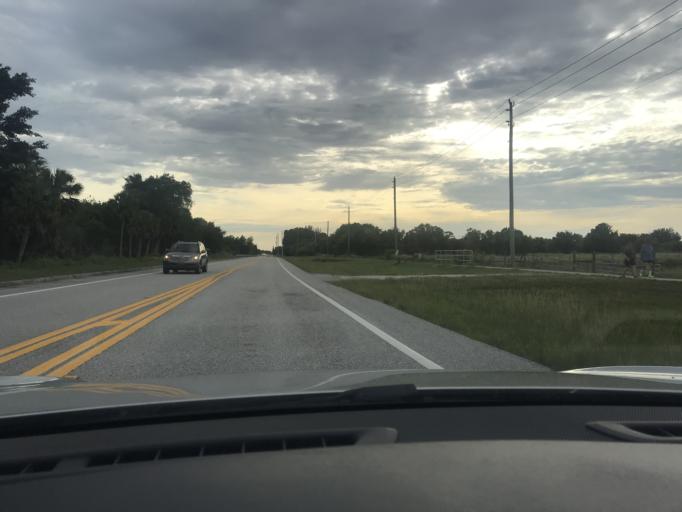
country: US
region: Florida
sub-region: Indian River County
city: West Vero Corridor
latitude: 27.6317
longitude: -80.4655
